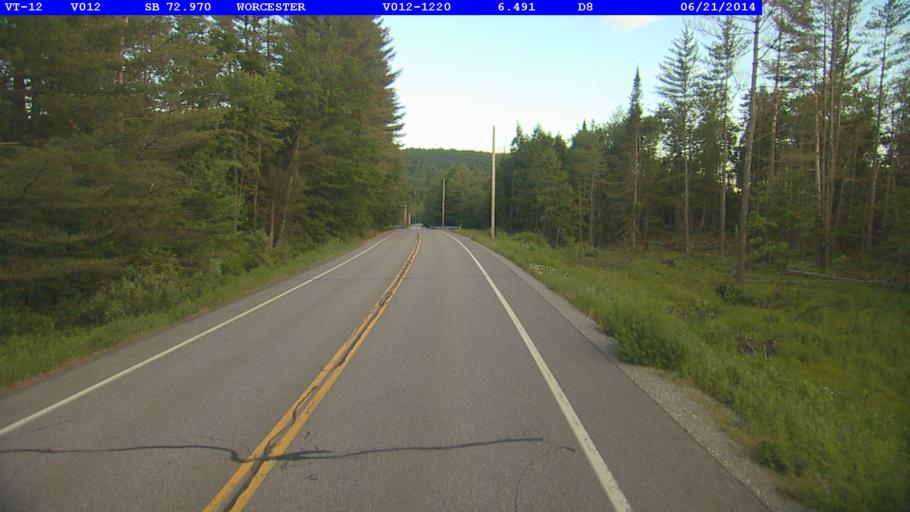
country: US
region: Vermont
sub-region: Lamoille County
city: Morrisville
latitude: 44.4349
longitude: -72.5357
